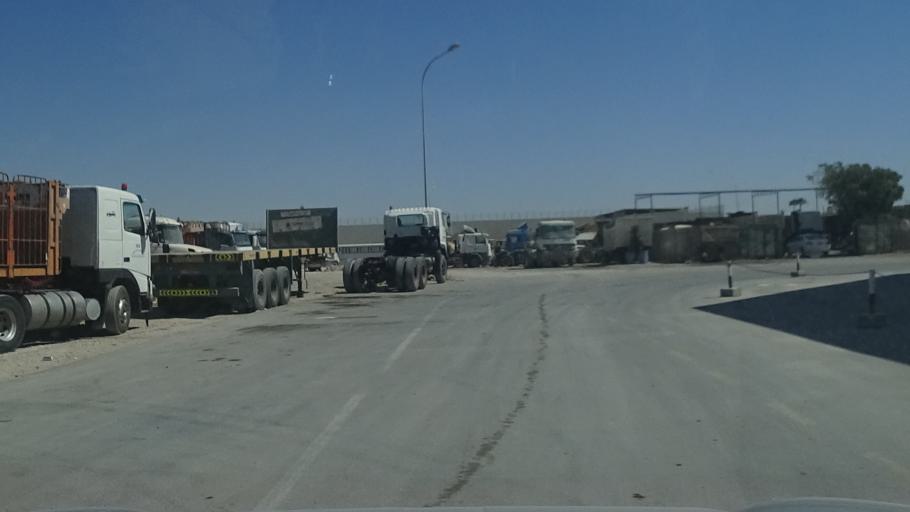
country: OM
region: Zufar
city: Salalah
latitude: 17.0341
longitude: 54.0407
